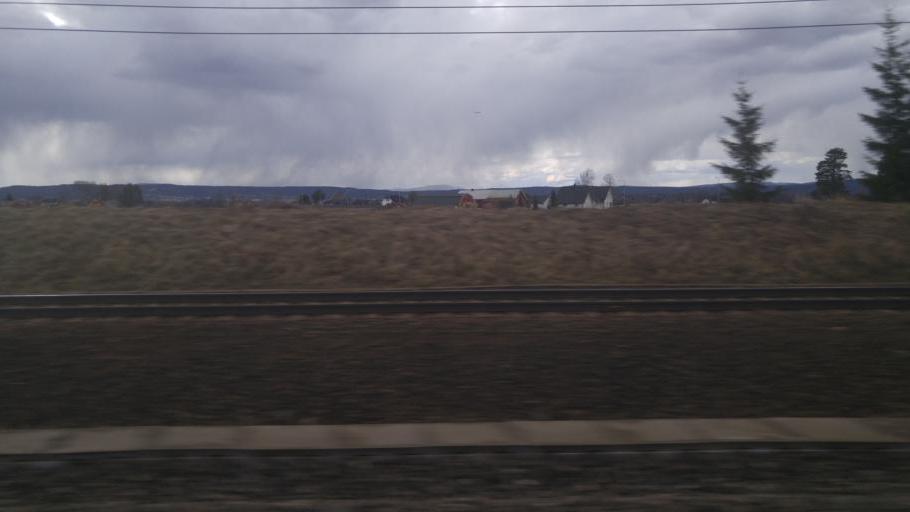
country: NO
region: Akershus
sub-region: Ullensaker
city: Klofta
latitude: 60.0907
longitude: 11.1405
